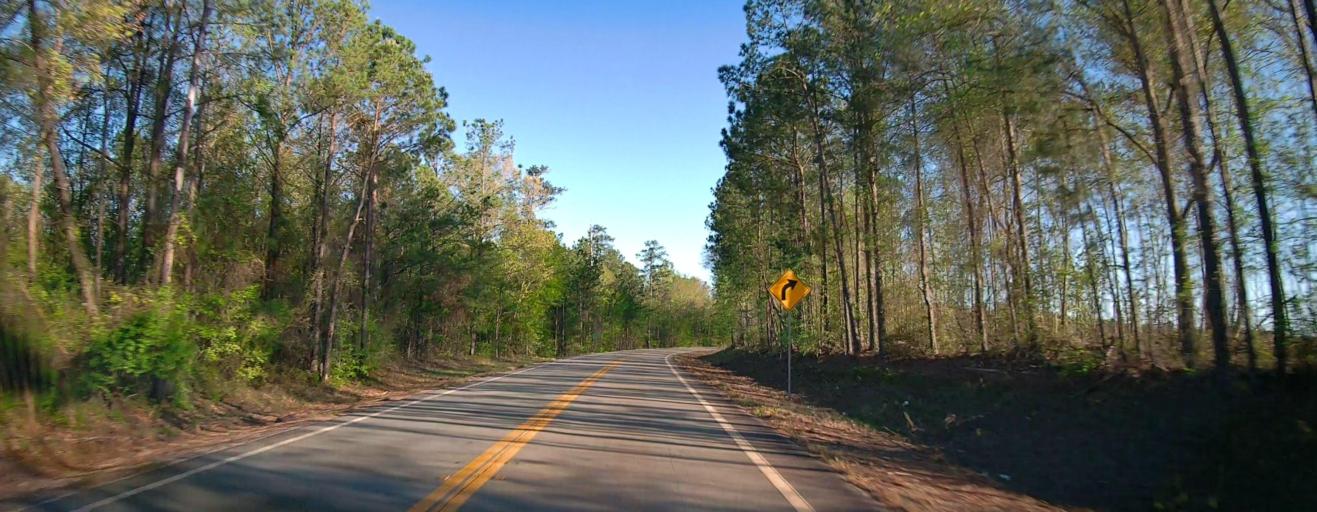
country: US
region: Georgia
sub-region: Wilkinson County
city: Irwinton
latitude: 32.8499
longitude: -83.0629
